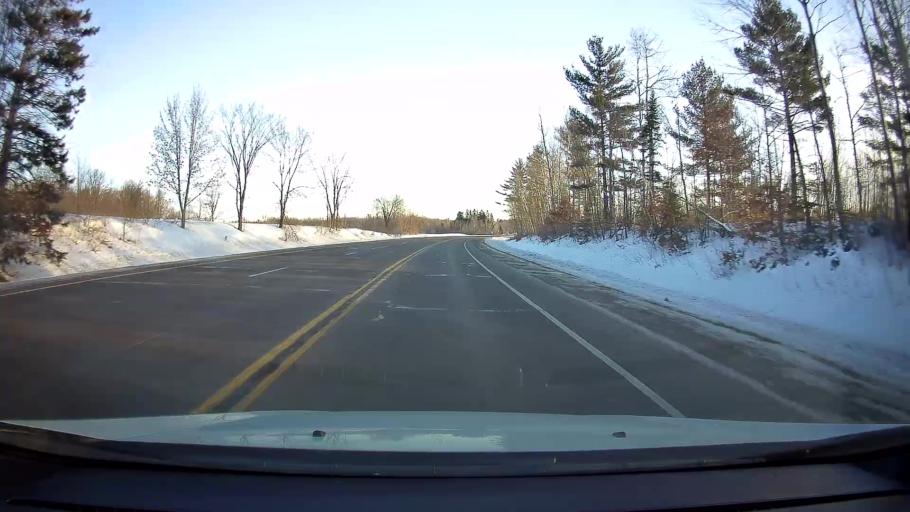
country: US
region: Wisconsin
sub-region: Barron County
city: Turtle Lake
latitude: 45.4622
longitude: -92.0985
